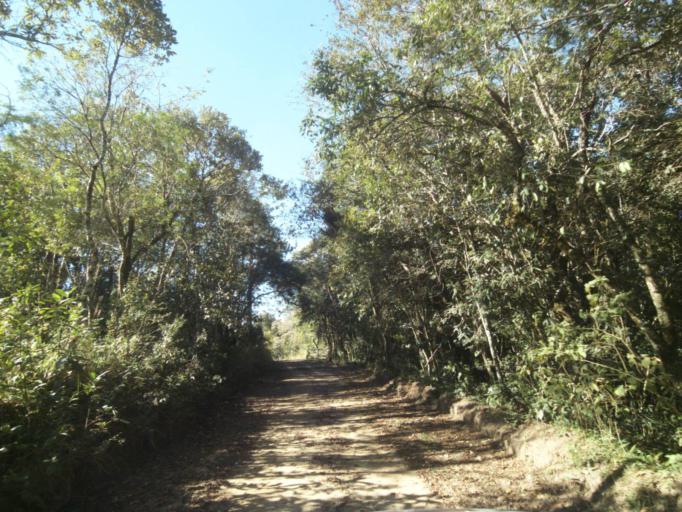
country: BR
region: Parana
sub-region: Tibagi
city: Tibagi
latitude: -24.5793
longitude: -50.4806
